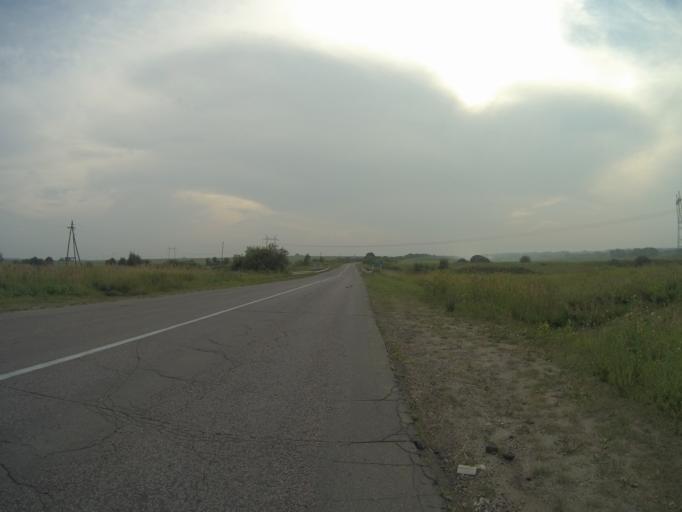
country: RU
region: Vladimir
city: Suzdal'
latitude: 56.3921
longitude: 40.3180
